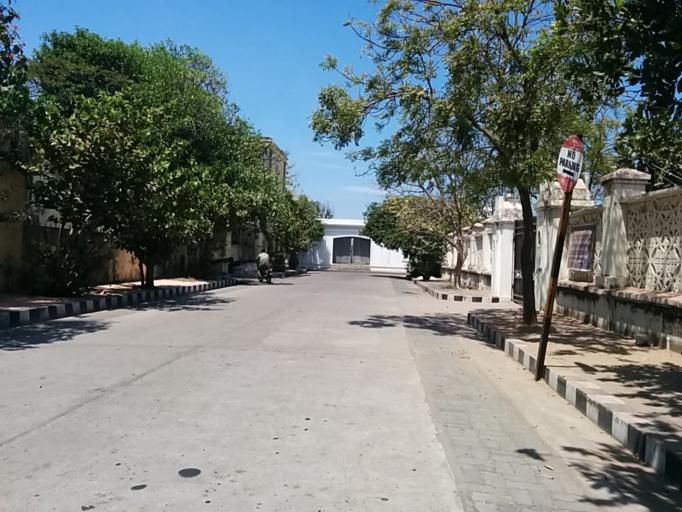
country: IN
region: Pondicherry
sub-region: Puducherry
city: Puducherry
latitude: 11.9312
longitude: 79.8350
